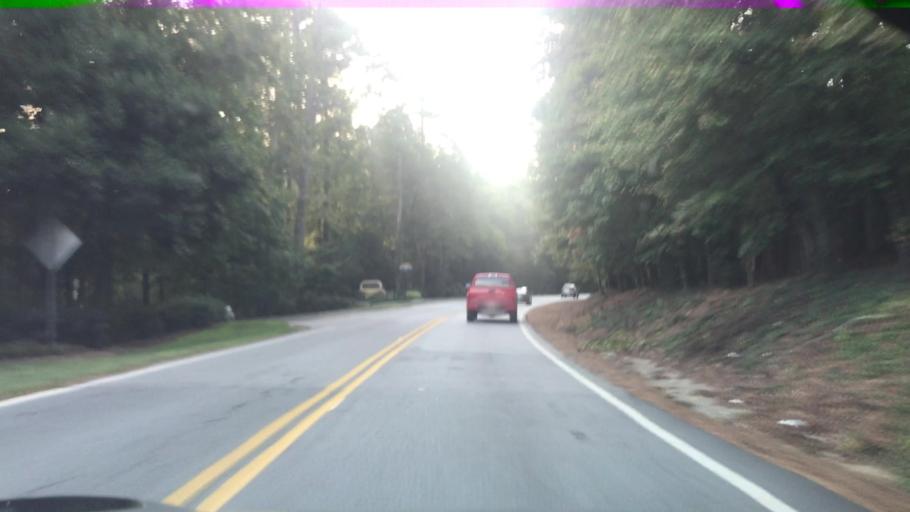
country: US
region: Georgia
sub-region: Gwinnett County
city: Suwanee
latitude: 34.0532
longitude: -84.0916
